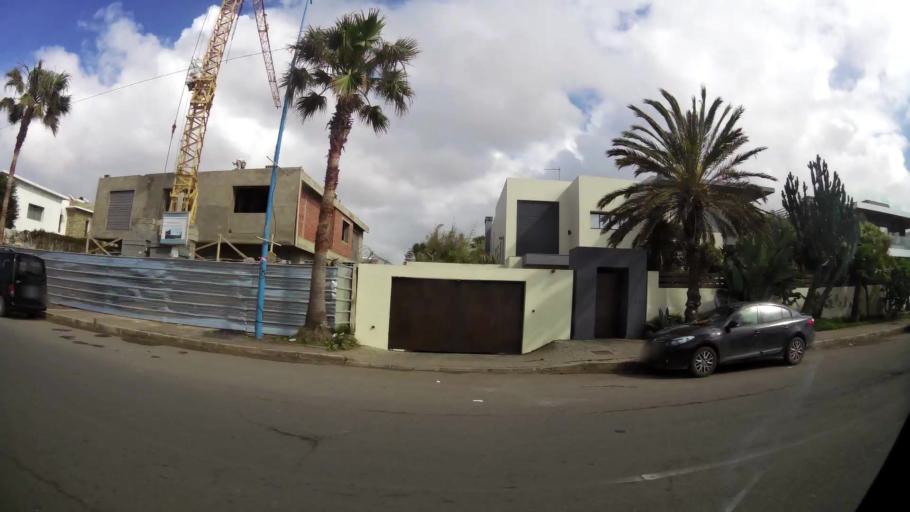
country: MA
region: Grand Casablanca
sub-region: Casablanca
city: Casablanca
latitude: 33.5718
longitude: -7.7079
